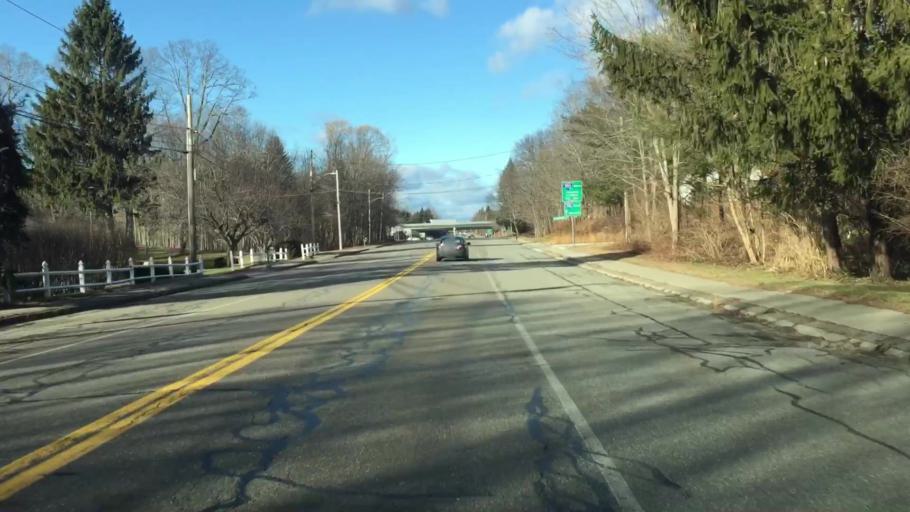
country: US
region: Massachusetts
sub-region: Worcester County
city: West Boylston
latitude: 42.3990
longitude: -71.7955
